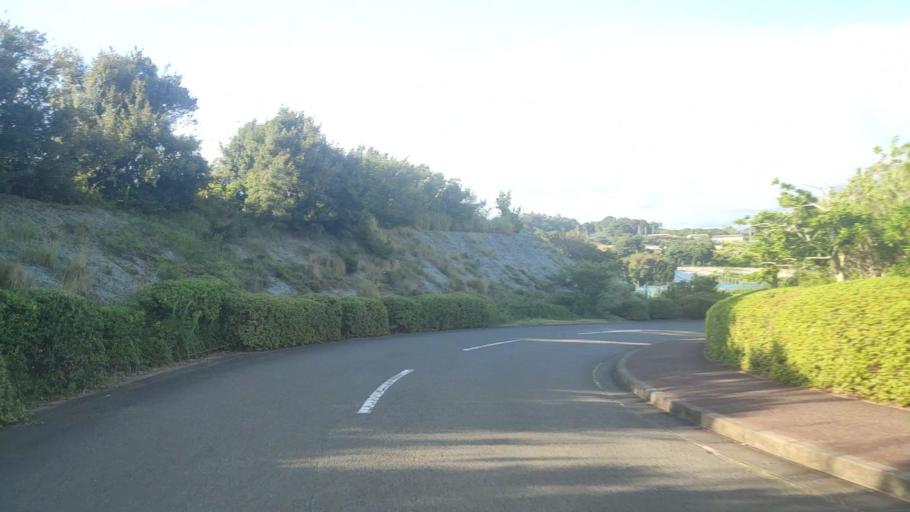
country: JP
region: Wakayama
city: Tanabe
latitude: 33.7693
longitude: 135.3024
